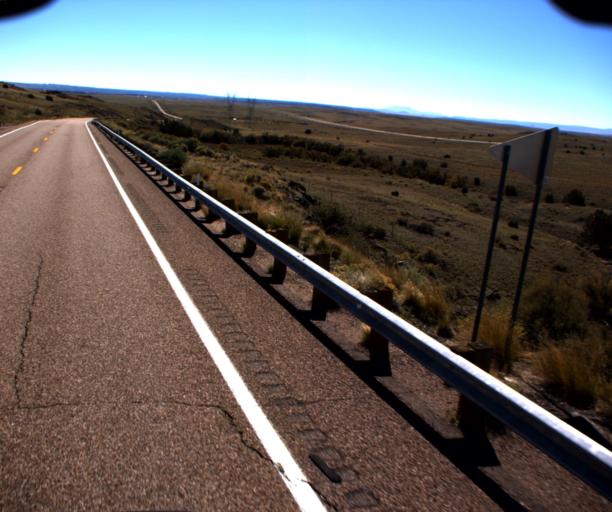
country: US
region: Arizona
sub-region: Apache County
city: Saint Johns
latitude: 34.5573
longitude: -109.4957
